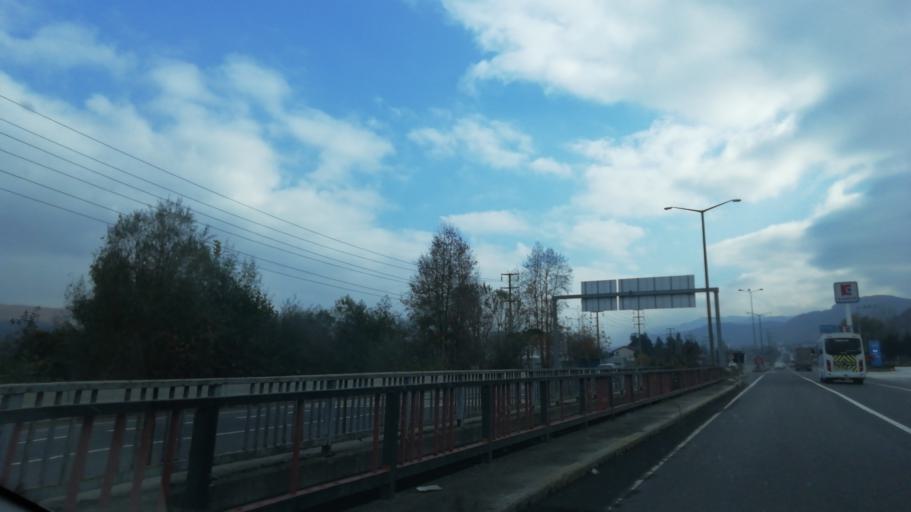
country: TR
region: Duzce
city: Kaynasli
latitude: 40.7817
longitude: 31.2779
